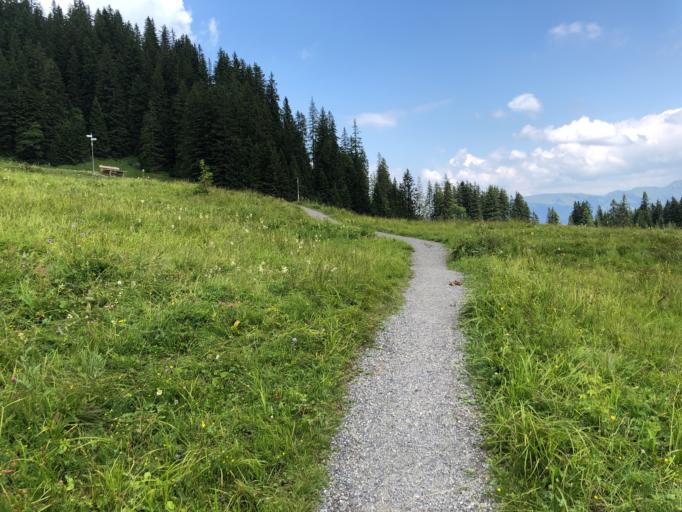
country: AT
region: Vorarlberg
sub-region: Politischer Bezirk Bregenz
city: Damuels
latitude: 47.3260
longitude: 9.8808
